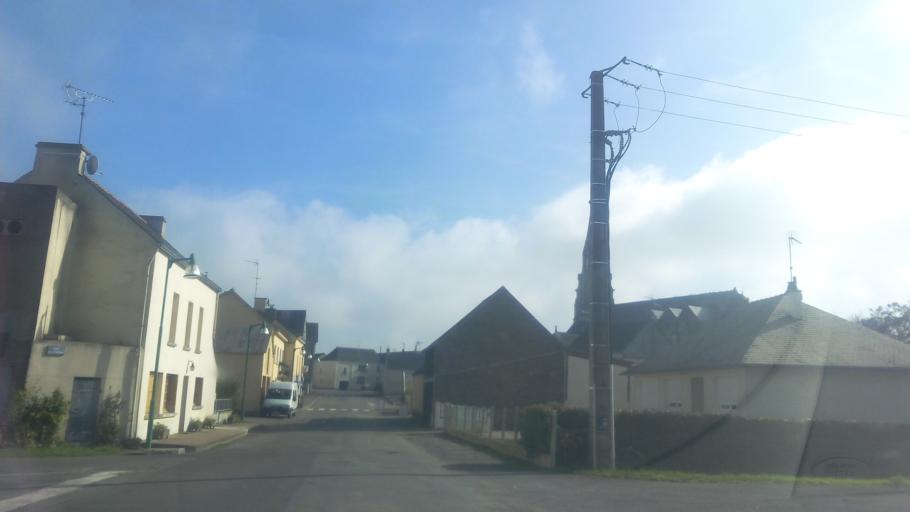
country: FR
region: Pays de la Loire
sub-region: Departement de la Loire-Atlantique
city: Conquereuil
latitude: 47.6254
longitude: -1.7527
